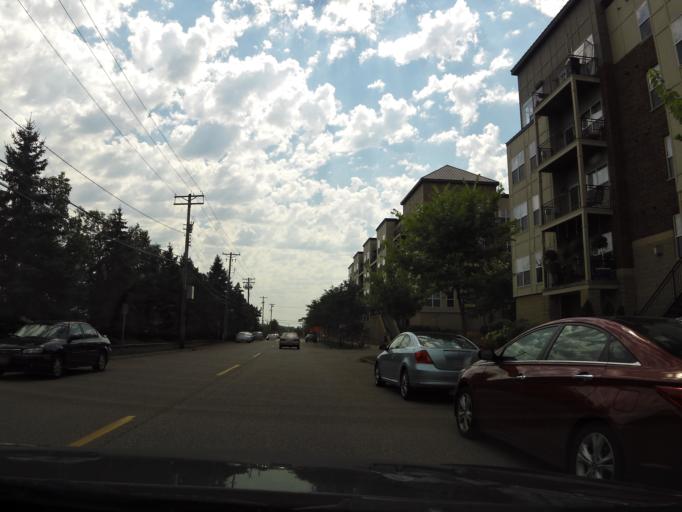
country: US
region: Minnesota
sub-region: Dakota County
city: Mendota Heights
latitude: 44.8994
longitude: -93.1722
